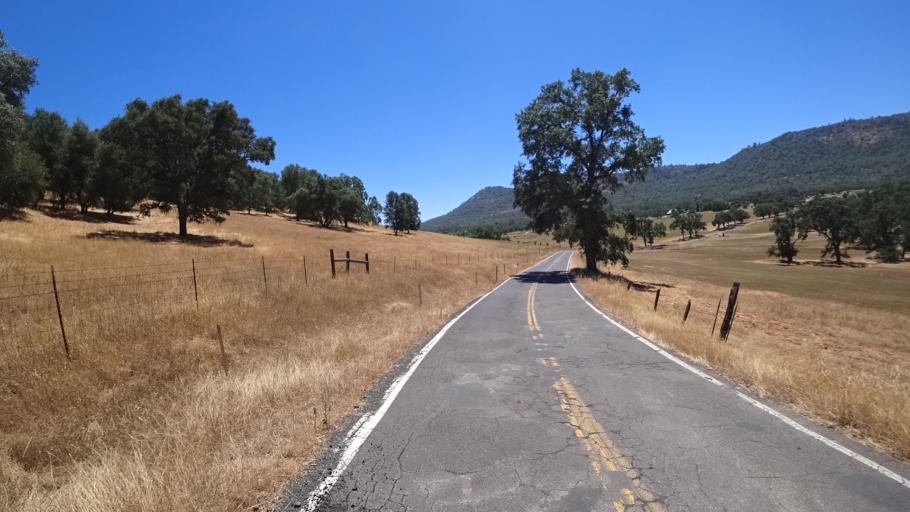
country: US
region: California
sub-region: Calaveras County
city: Copperopolis
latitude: 38.0832
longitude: -120.6617
